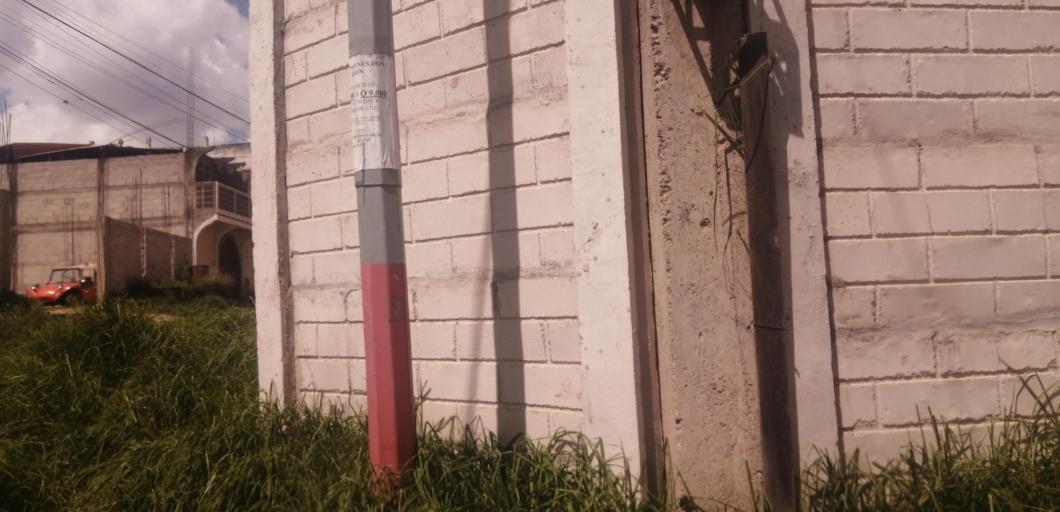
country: GT
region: Quetzaltenango
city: Quetzaltenango
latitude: 14.8295
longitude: -91.5326
